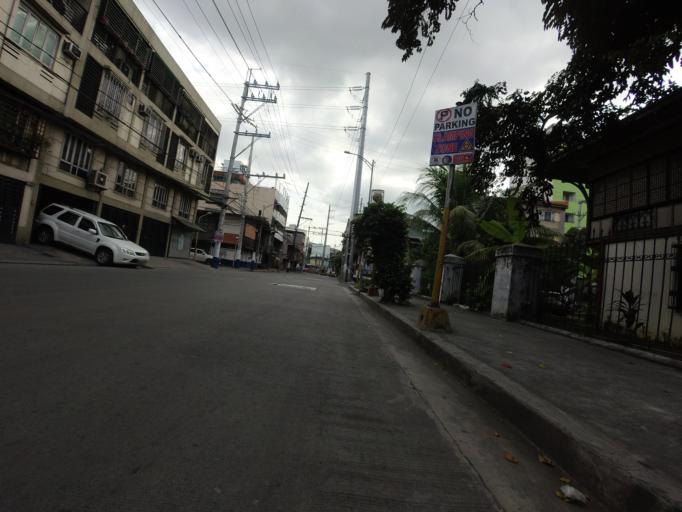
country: PH
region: Metro Manila
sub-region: City of Manila
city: Quiapo
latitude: 14.5797
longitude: 120.9974
